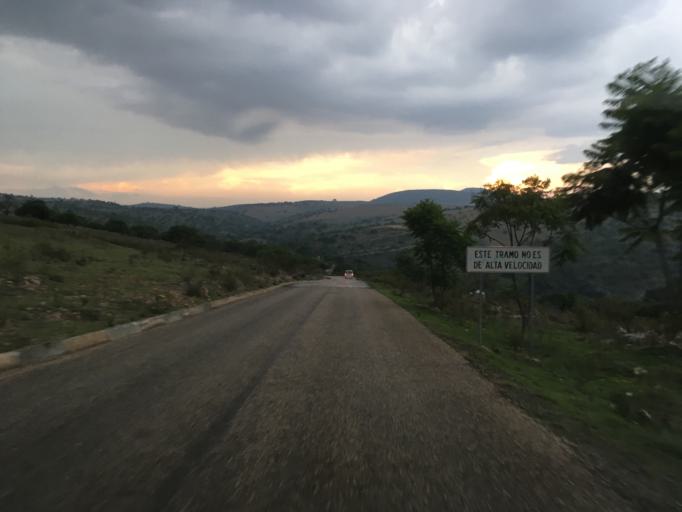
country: MX
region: Oaxaca
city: Santiago Tilantongo
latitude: 17.2892
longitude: -97.2775
